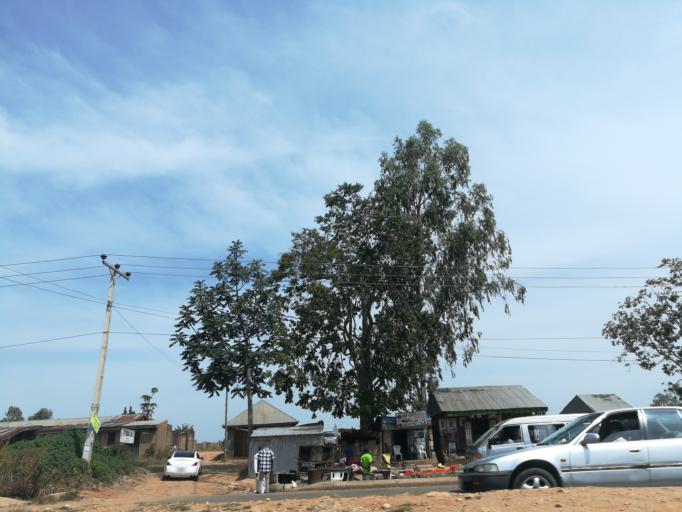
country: NG
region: Plateau
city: Bukuru
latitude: 9.8195
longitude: 8.8654
